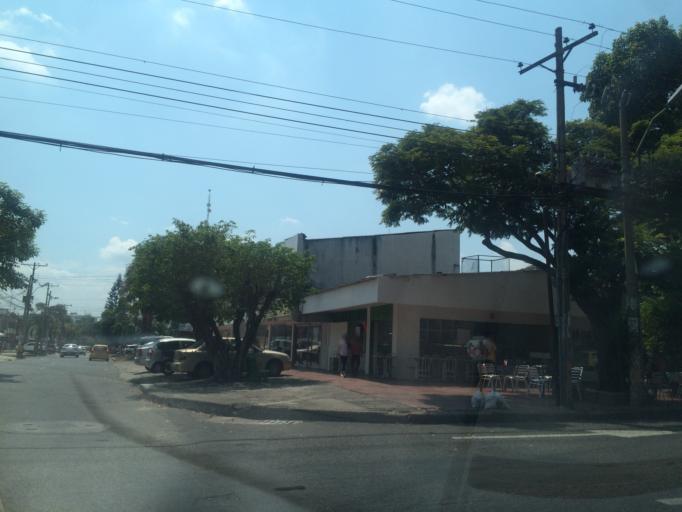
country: CO
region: Valle del Cauca
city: Cali
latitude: 3.4677
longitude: -76.5271
